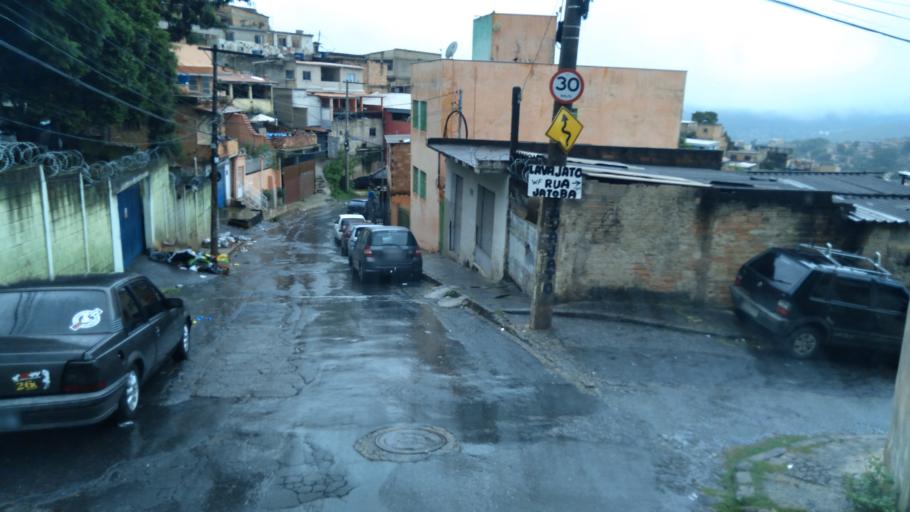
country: BR
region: Minas Gerais
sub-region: Belo Horizonte
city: Belo Horizonte
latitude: -19.9193
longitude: -43.8771
